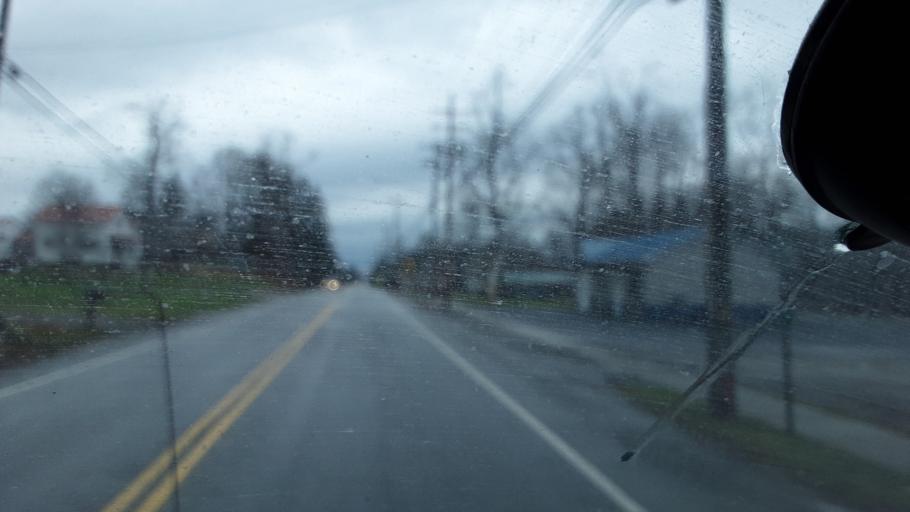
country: US
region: New York
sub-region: Erie County
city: Holland
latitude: 42.6477
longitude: -78.5490
